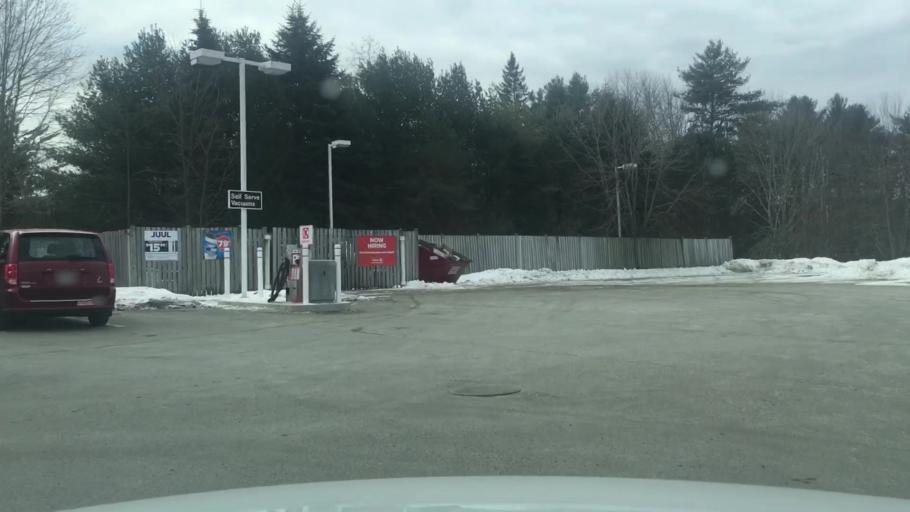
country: US
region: Maine
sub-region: Lincoln County
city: Waldoboro
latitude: 44.1017
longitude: -69.3811
